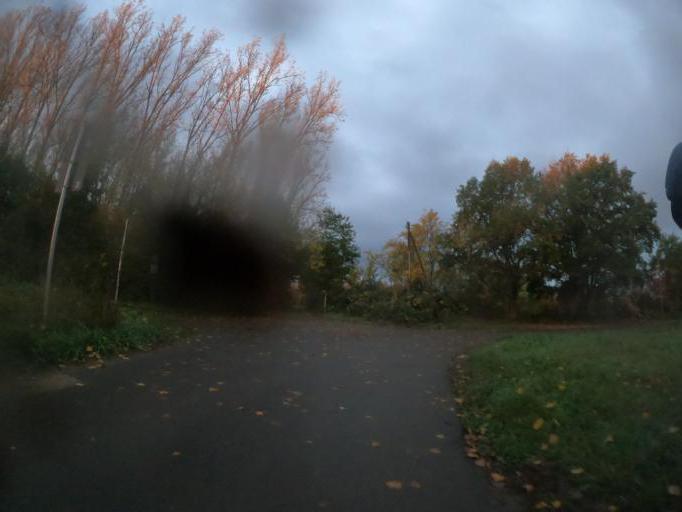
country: DE
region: Hesse
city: Dreieich
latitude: 50.0253
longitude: 8.7166
